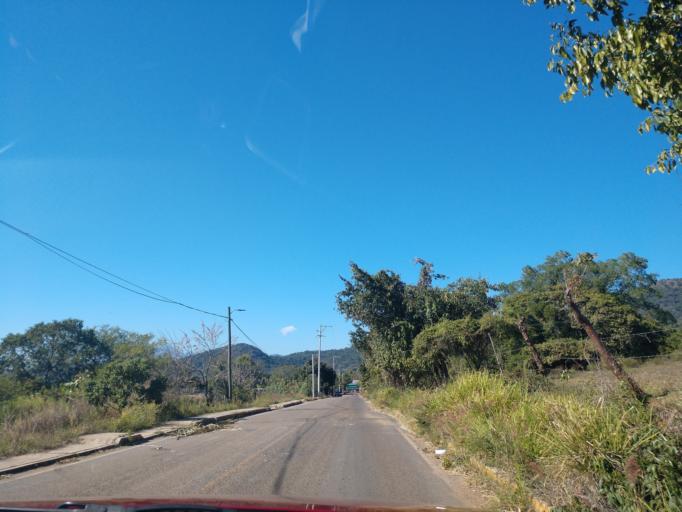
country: MX
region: Nayarit
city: Compostela
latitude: 21.2813
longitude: -104.8767
